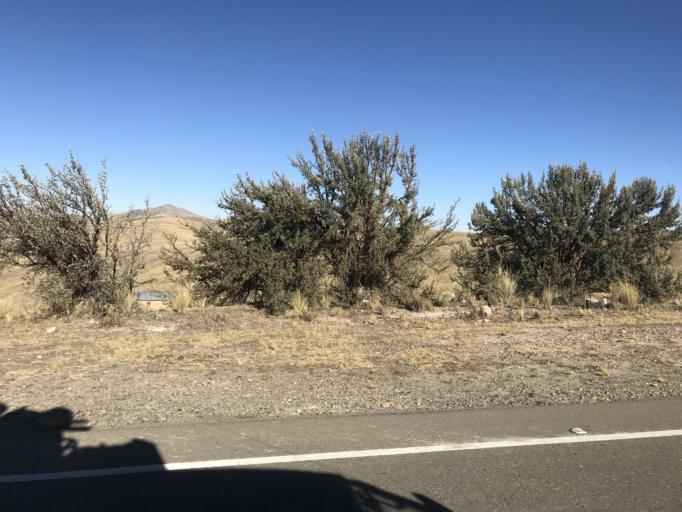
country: PE
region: Puno
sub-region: Yunguyo
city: Yunguyo
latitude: -16.1655
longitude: -68.9858
